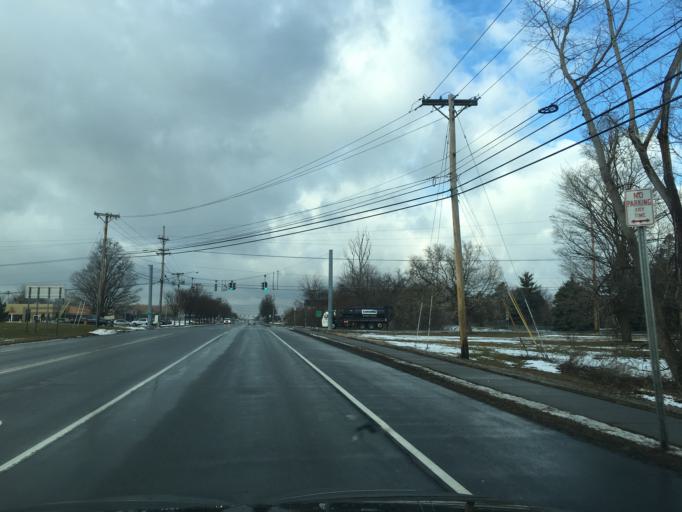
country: US
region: New York
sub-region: Ontario County
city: Victor
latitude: 42.9745
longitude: -77.3478
